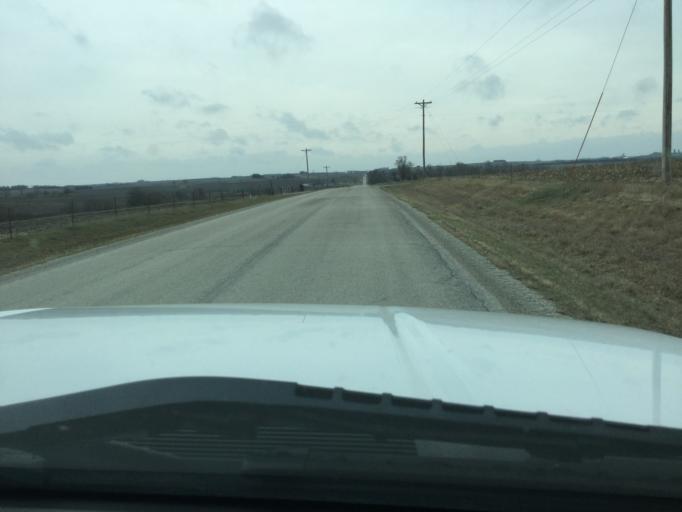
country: US
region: Kansas
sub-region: Nemaha County
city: Sabetha
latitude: 39.8691
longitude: -95.7141
